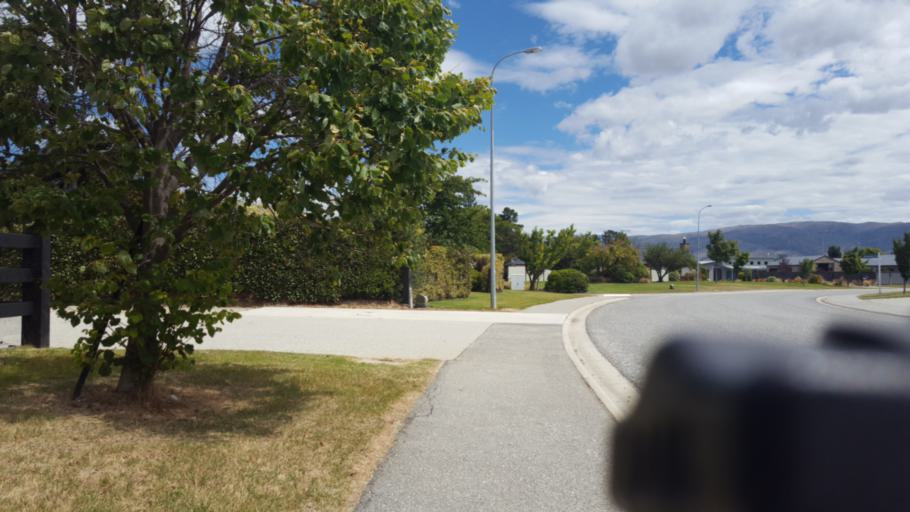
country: NZ
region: Otago
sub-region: Queenstown-Lakes District
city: Wanaka
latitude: -45.0398
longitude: 169.2180
